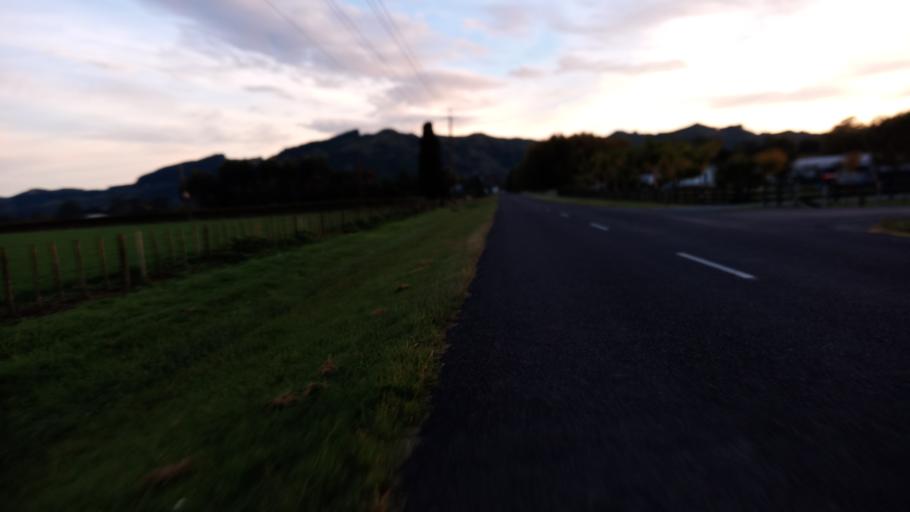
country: NZ
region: Gisborne
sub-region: Gisborne District
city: Gisborne
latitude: -38.6249
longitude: 177.9781
